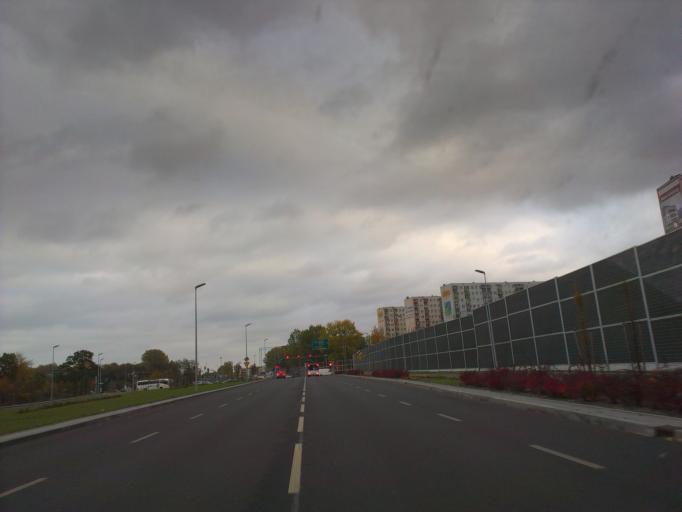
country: PL
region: Kujawsko-Pomorskie
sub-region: Torun
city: Torun
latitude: 53.0270
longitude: 18.6079
